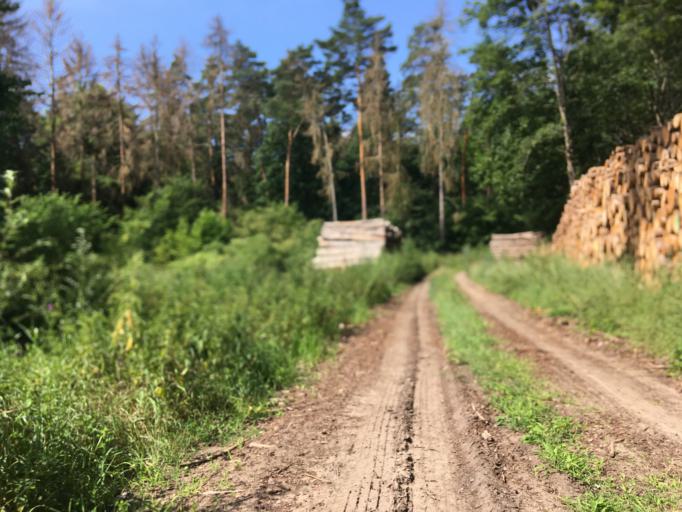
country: DE
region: Brandenburg
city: Casekow
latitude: 53.2299
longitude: 14.1336
